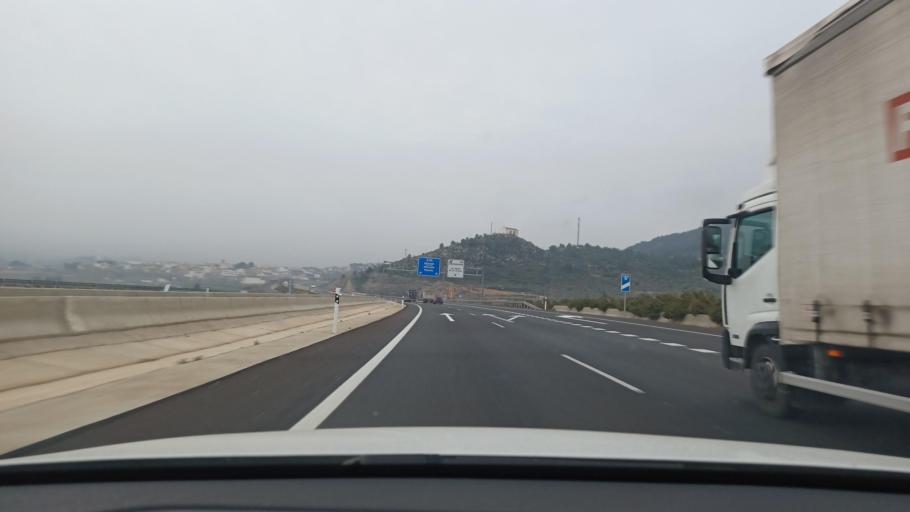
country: ES
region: Valencia
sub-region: Provincia de Valencia
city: La Font de la Figuera
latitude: 38.8197
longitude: -0.8905
